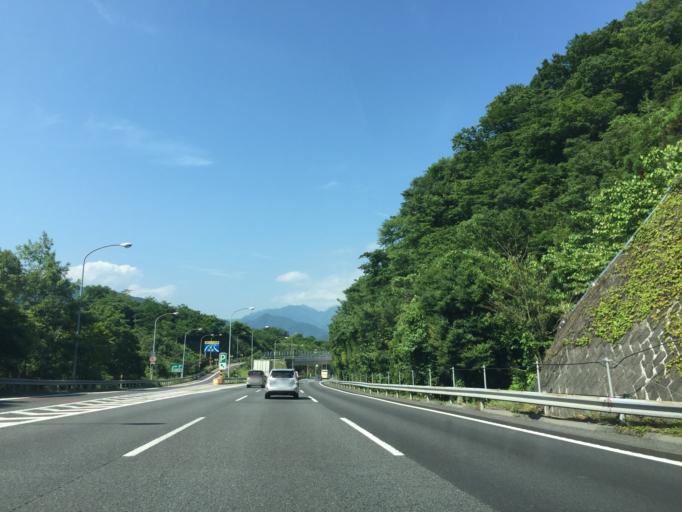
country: JP
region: Shizuoka
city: Gotemba
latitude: 35.3539
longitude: 139.0125
